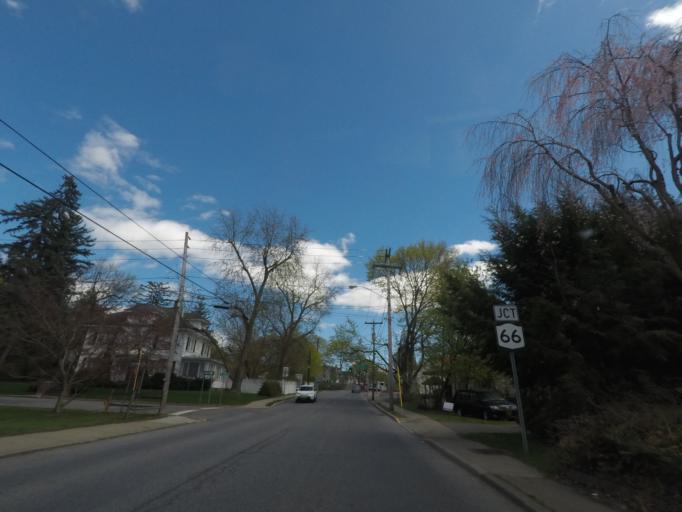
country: US
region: New York
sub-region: Columbia County
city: Oakdale
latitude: 42.2470
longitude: -73.7725
